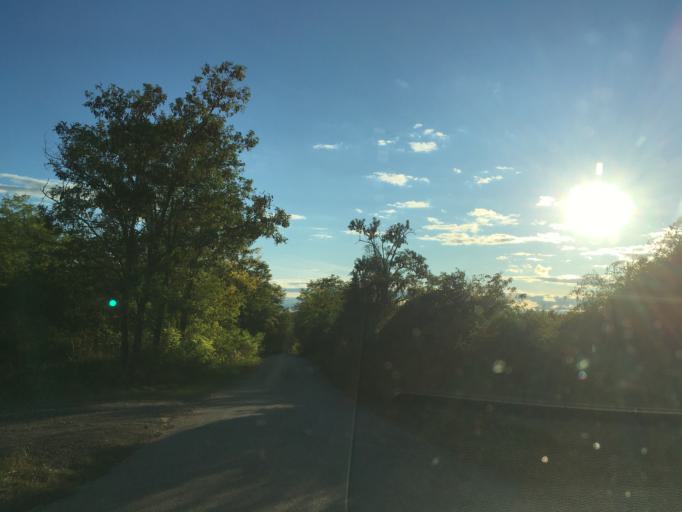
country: SK
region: Nitriansky
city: Svodin
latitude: 47.9163
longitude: 18.4343
